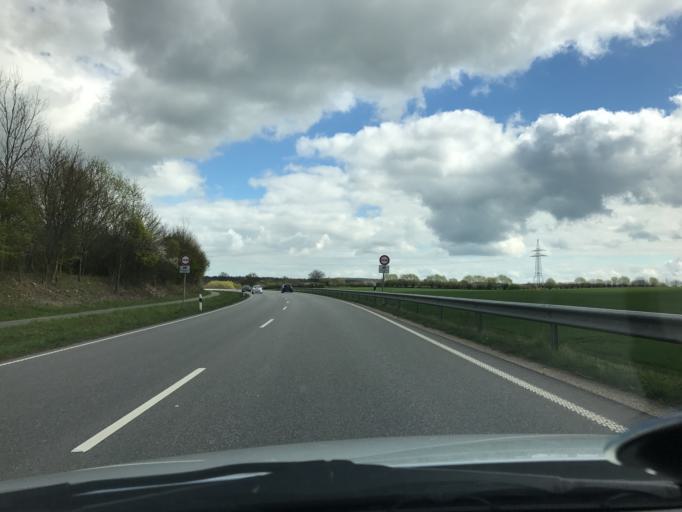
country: DE
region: Schleswig-Holstein
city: Eutin
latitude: 54.1153
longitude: 10.6229
